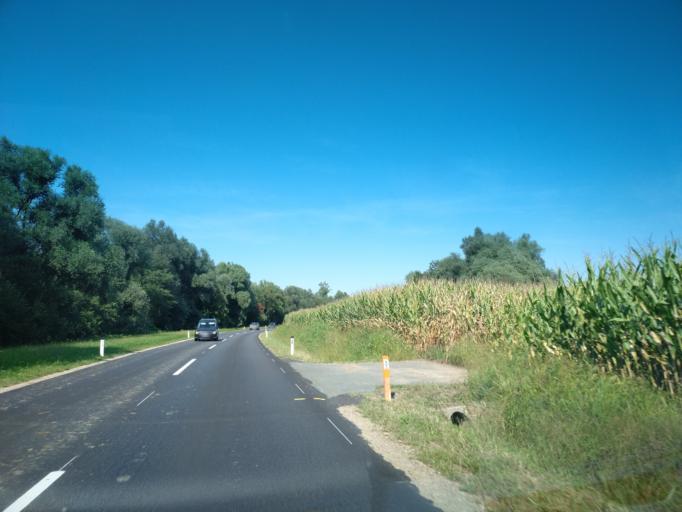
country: AT
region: Styria
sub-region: Politischer Bezirk Leibnitz
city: Sankt Johann im Saggautal
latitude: 46.7108
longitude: 15.3996
